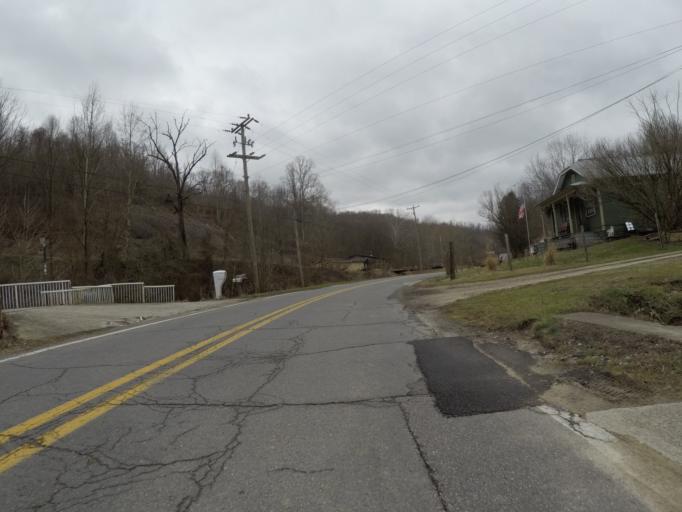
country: US
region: West Virginia
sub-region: Cabell County
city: Lesage
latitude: 38.4702
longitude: -82.2844
